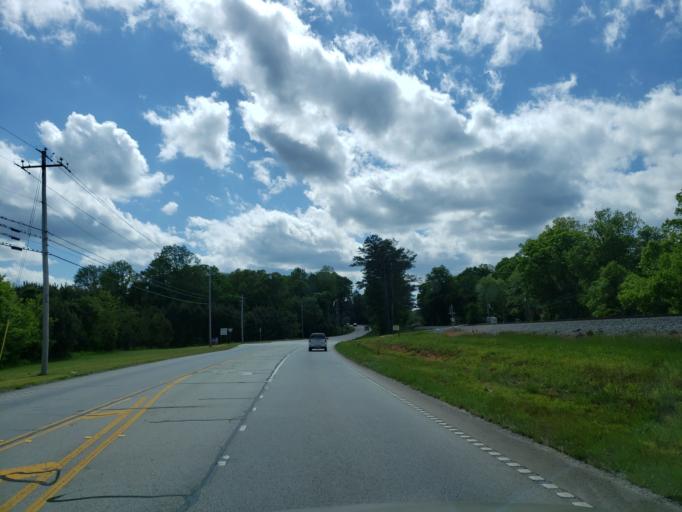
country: US
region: Georgia
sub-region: Haralson County
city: Bremen
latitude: 33.7076
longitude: -85.1697
